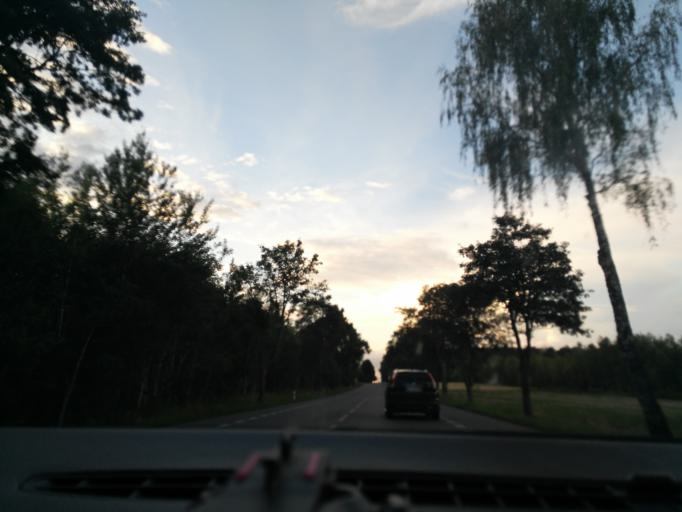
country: PL
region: Lublin Voivodeship
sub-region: Powiat lubelski
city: Niemce
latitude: 51.3892
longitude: 22.6359
